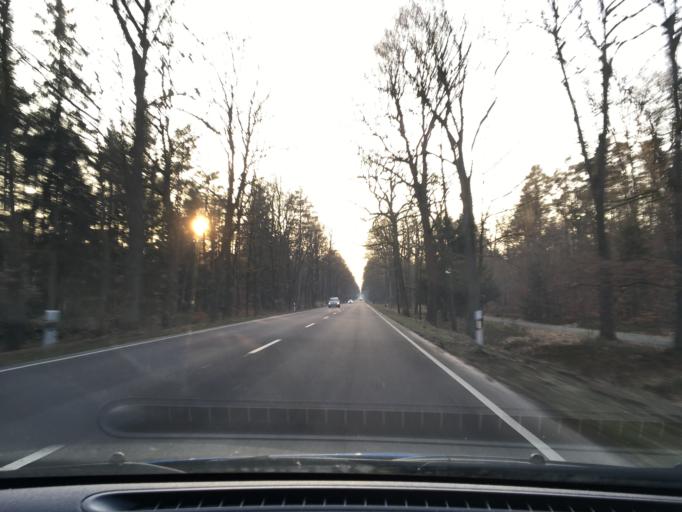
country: DE
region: Lower Saxony
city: Sprakensehl
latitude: 52.8281
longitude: 10.4722
